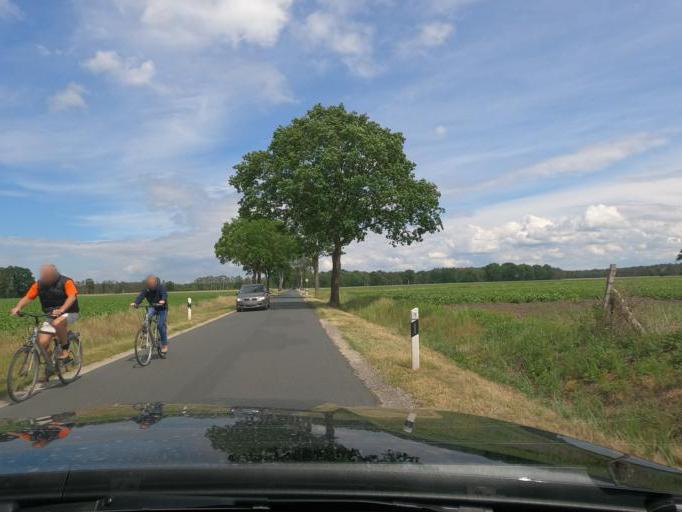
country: DE
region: Lower Saxony
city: Lindwedel
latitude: 52.6082
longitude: 9.6241
